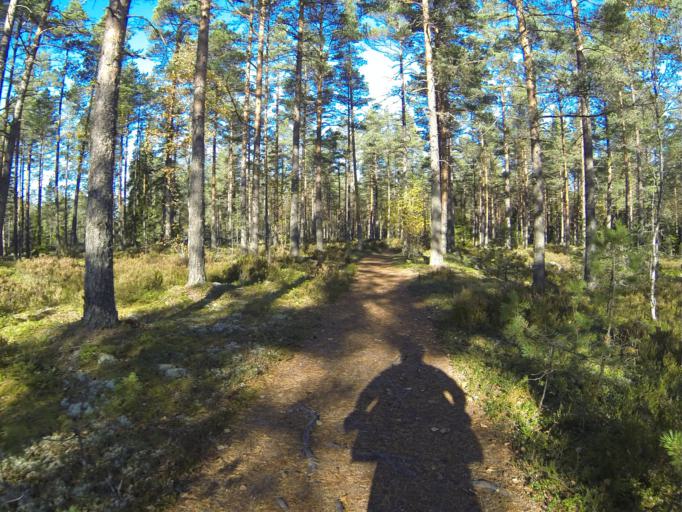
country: FI
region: Varsinais-Suomi
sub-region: Salo
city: Saerkisalo
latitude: 60.2042
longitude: 22.9221
